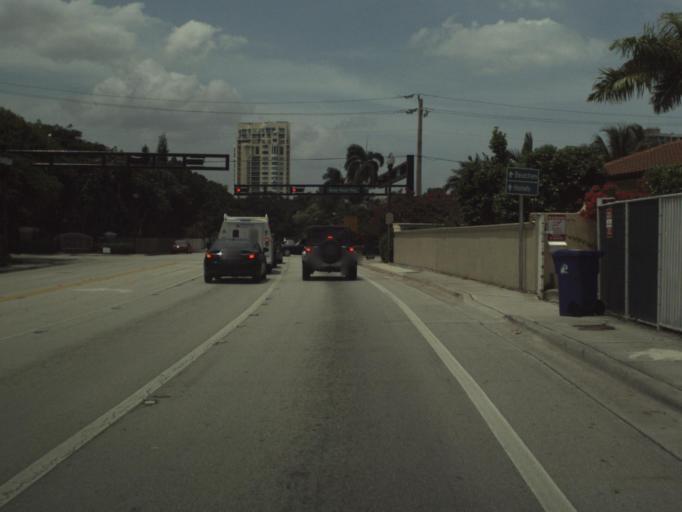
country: US
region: Florida
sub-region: Broward County
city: Sunrise
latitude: 26.1036
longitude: -80.1090
